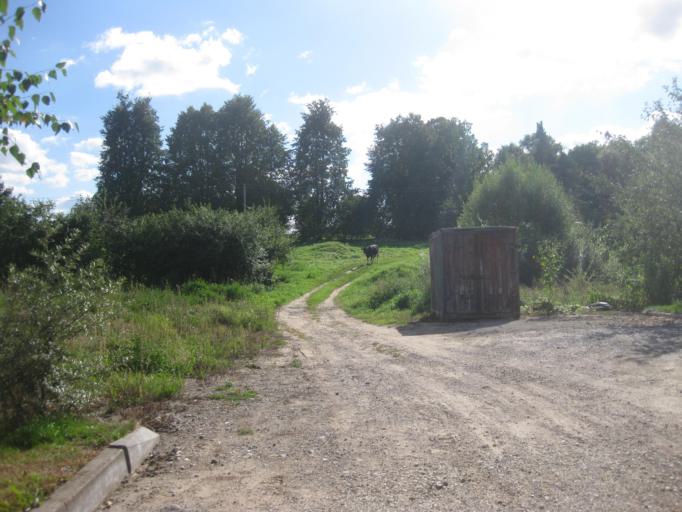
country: LT
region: Kauno apskritis
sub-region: Kauno rajonas
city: Garliava
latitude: 54.8330
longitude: 23.8641
